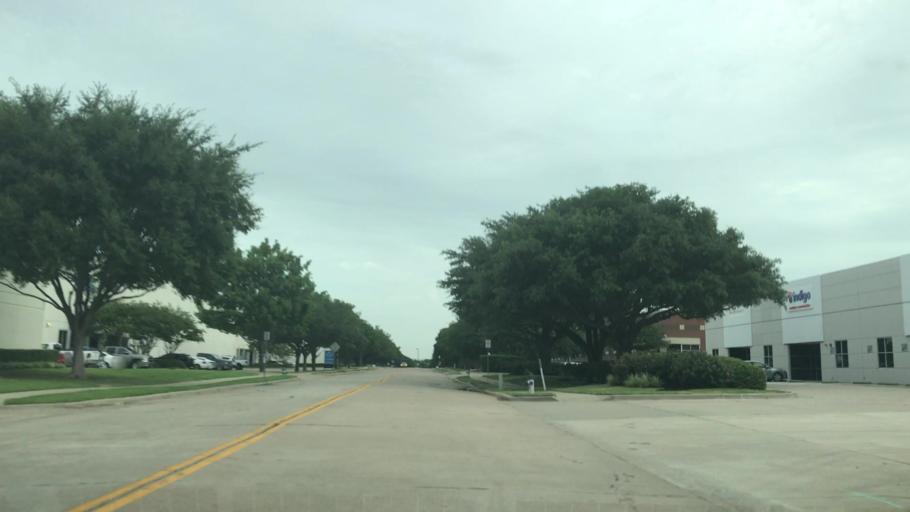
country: US
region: Texas
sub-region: Dallas County
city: Coppell
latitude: 32.9174
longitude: -97.0027
